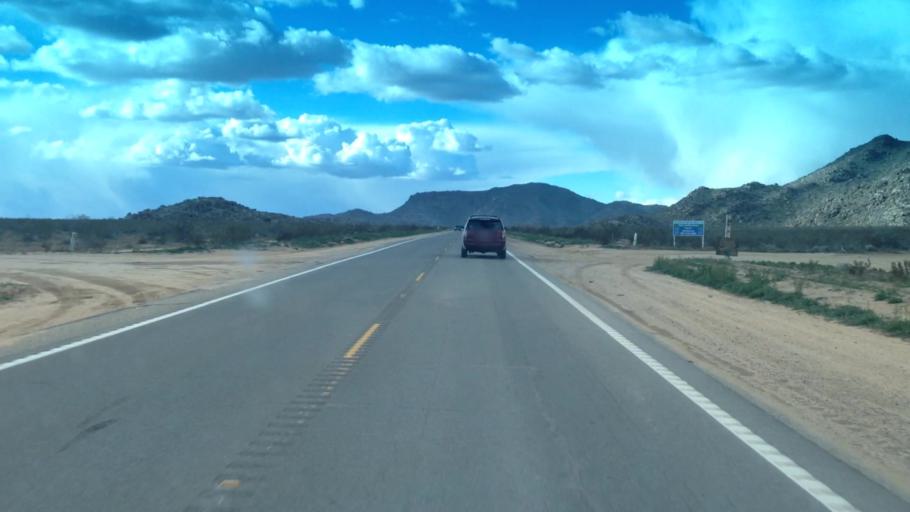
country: US
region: California
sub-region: San Bernardino County
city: Lucerne Valley
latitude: 34.4592
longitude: -117.0767
